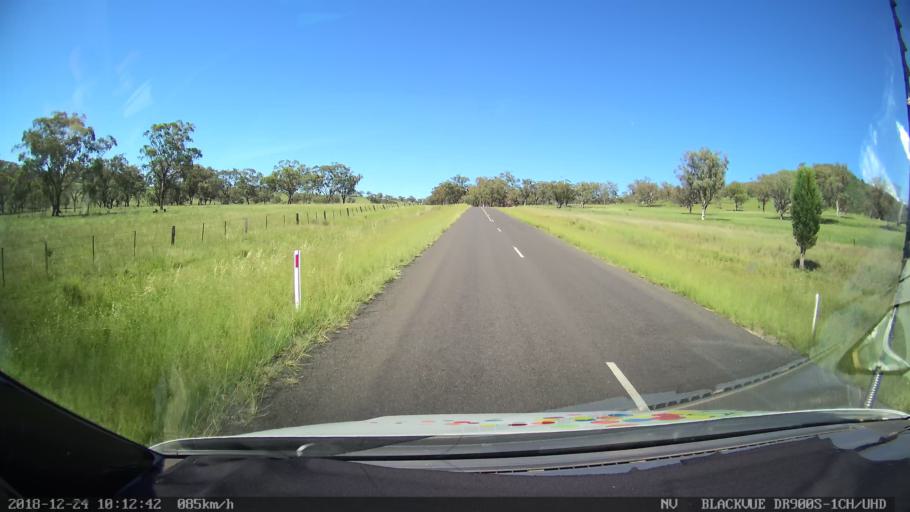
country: AU
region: New South Wales
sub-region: Liverpool Plains
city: Quirindi
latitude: -31.6818
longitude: 150.6454
